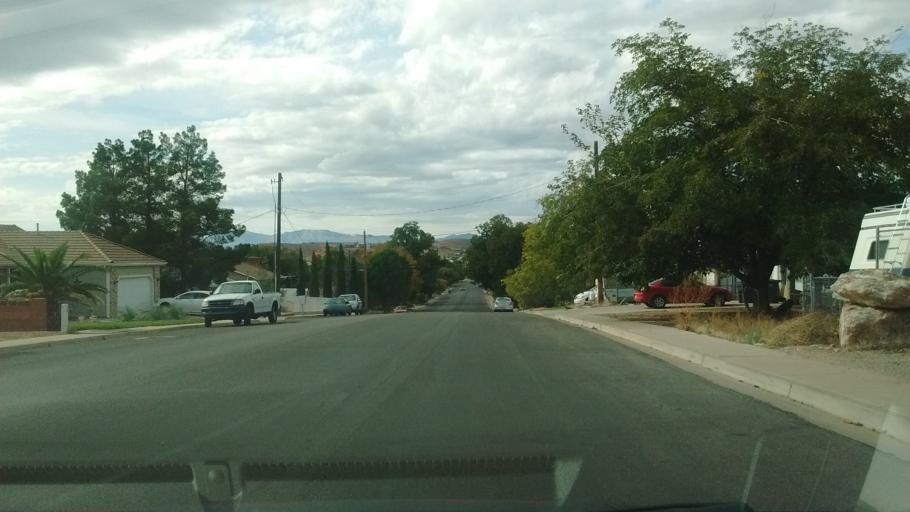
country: US
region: Utah
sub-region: Washington County
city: Washington
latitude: 37.1340
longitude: -113.5051
